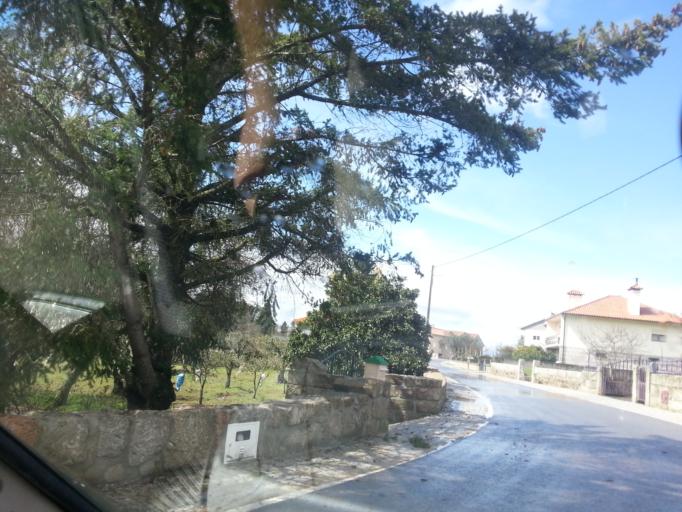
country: PT
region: Guarda
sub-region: Fornos de Algodres
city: Fornos de Algodres
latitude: 40.5828
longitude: -7.4745
